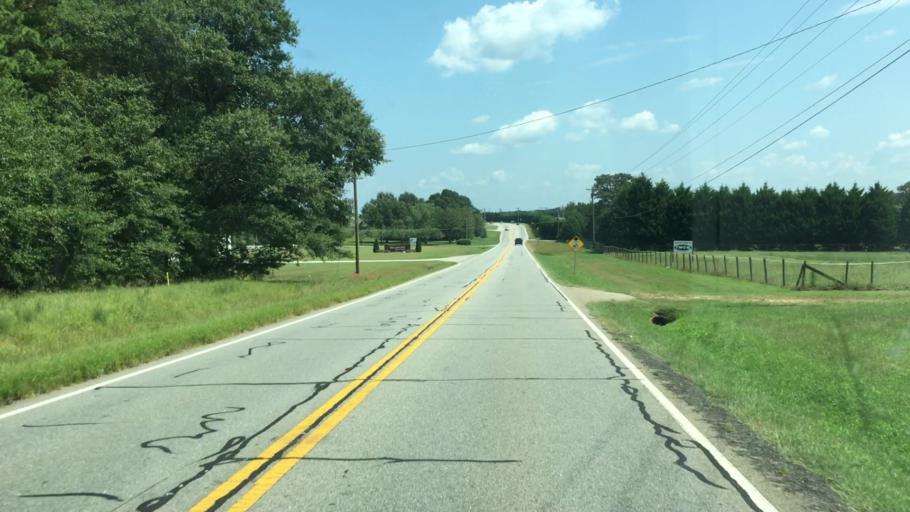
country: US
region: Georgia
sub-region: Oconee County
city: Watkinsville
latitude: 33.8666
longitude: -83.4670
